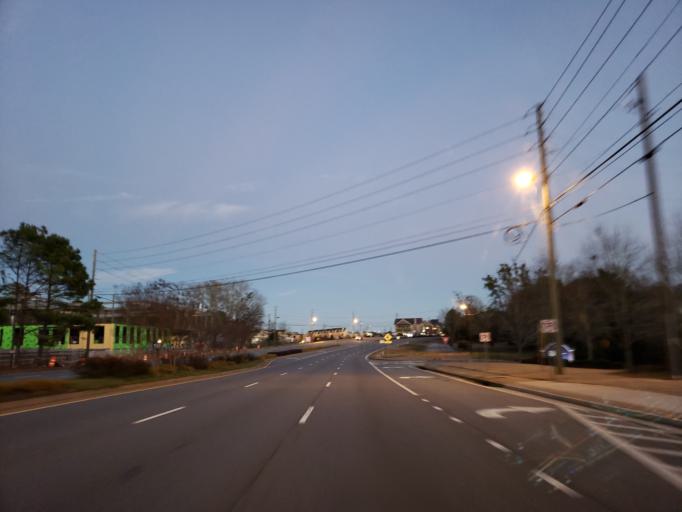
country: US
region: Georgia
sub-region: Fulton County
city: Alpharetta
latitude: 34.0704
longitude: -84.2889
